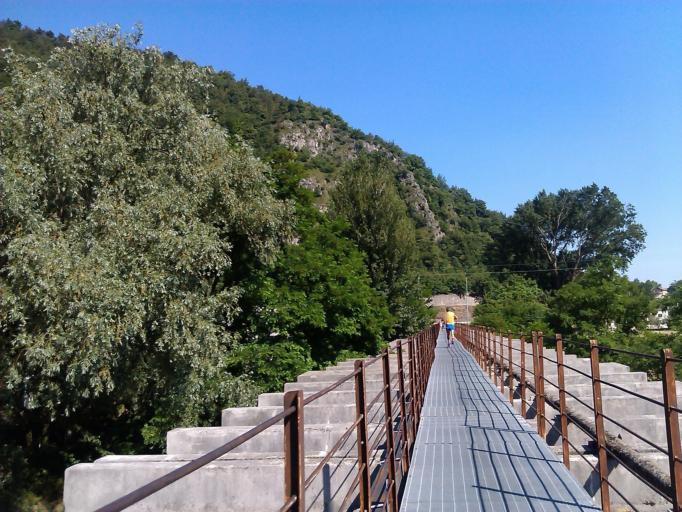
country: IT
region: Veneto
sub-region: Provincia di Vicenza
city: Campese
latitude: 45.8069
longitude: 11.7157
